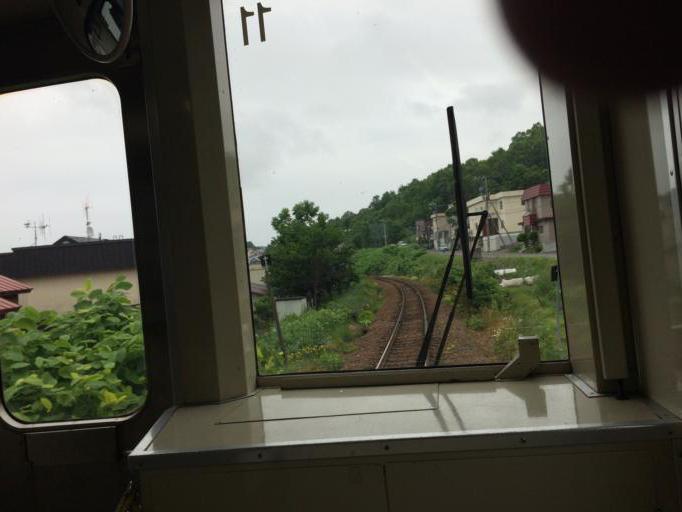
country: JP
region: Hokkaido
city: Otaru
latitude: 43.2085
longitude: 140.9689
